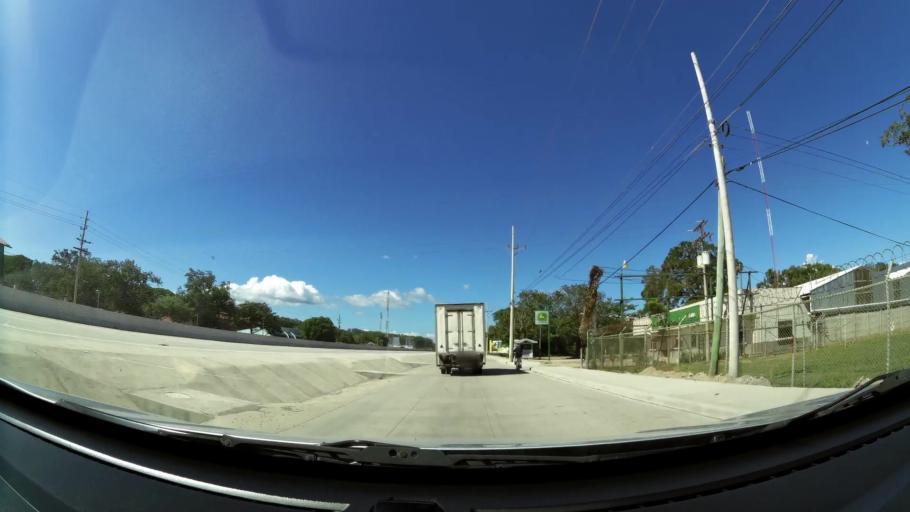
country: CR
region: Guanacaste
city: Liberia
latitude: 10.6156
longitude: -85.4363
